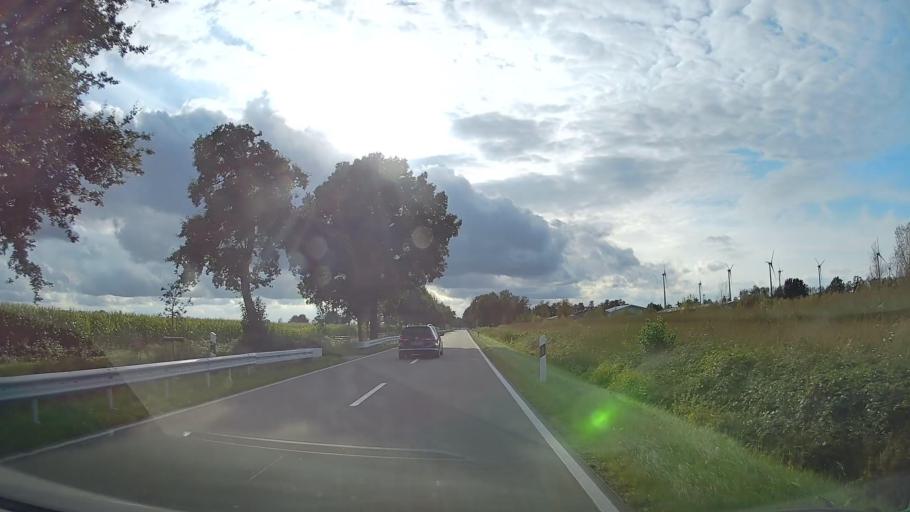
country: DE
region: Lower Saxony
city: Friesoythe
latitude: 53.0572
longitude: 7.7916
